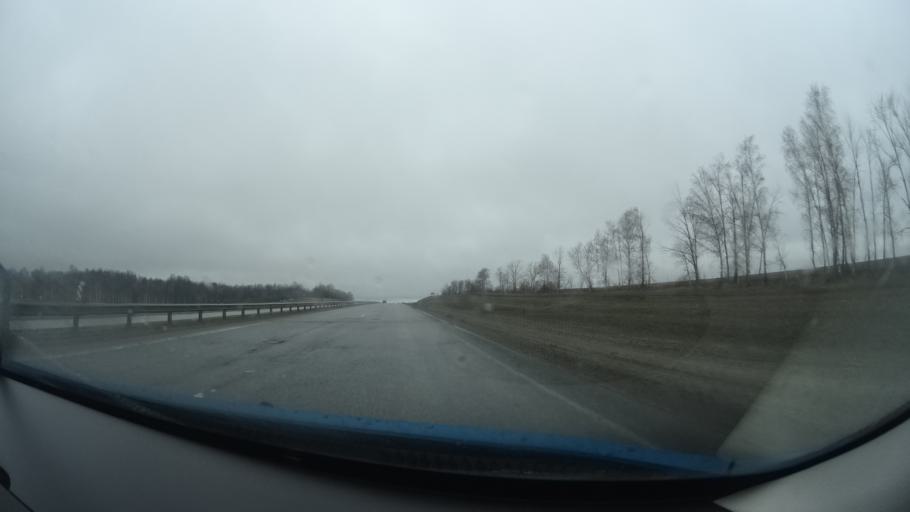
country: RU
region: Bashkortostan
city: Alekseyevka
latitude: 54.7336
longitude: 55.1282
